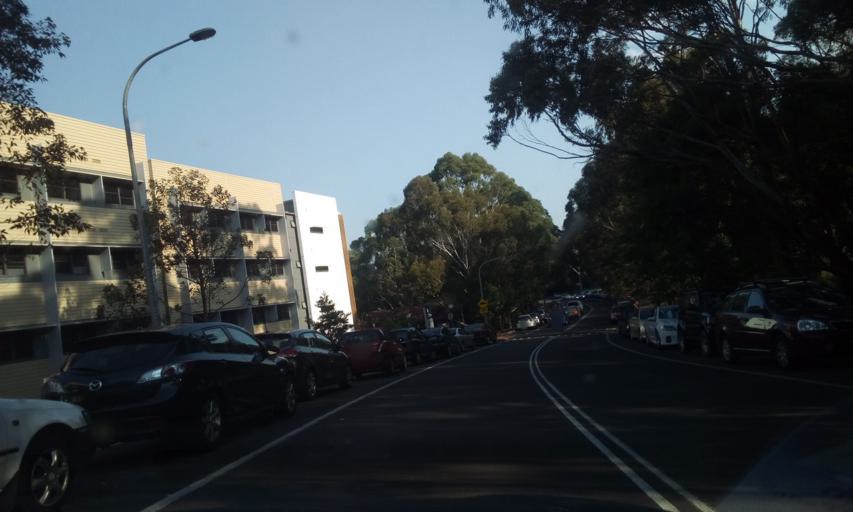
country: AU
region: New South Wales
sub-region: Wollongong
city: Mount Ousley
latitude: -34.4055
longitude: 150.8729
